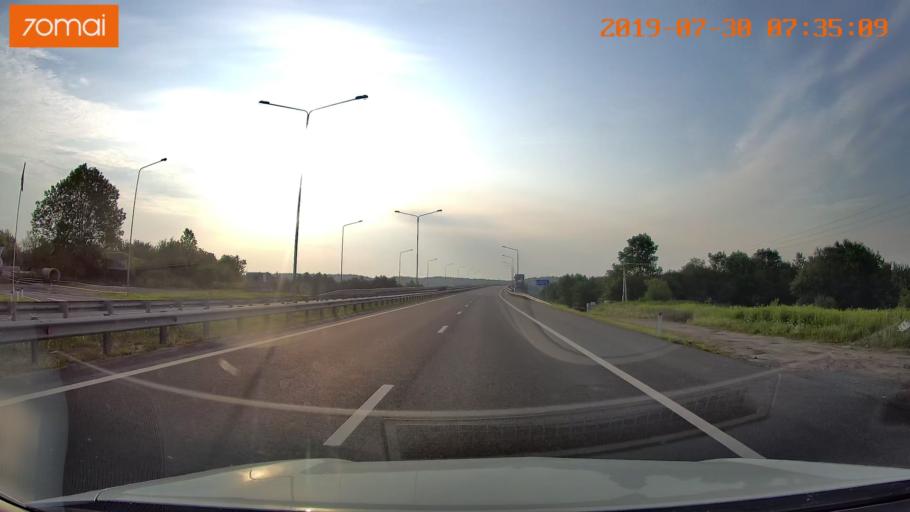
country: RU
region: Kaliningrad
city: Gvardeysk
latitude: 54.6723
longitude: 21.0919
